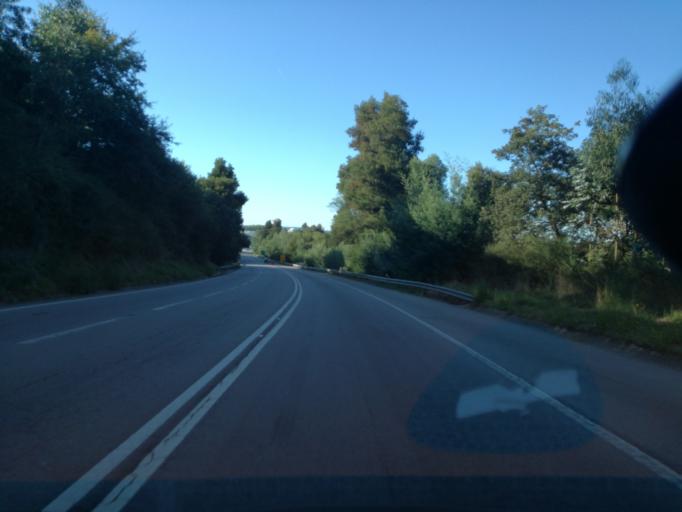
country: PT
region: Porto
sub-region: Santo Tirso
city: Sao Miguel do Couto
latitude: 41.3232
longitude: -8.4689
